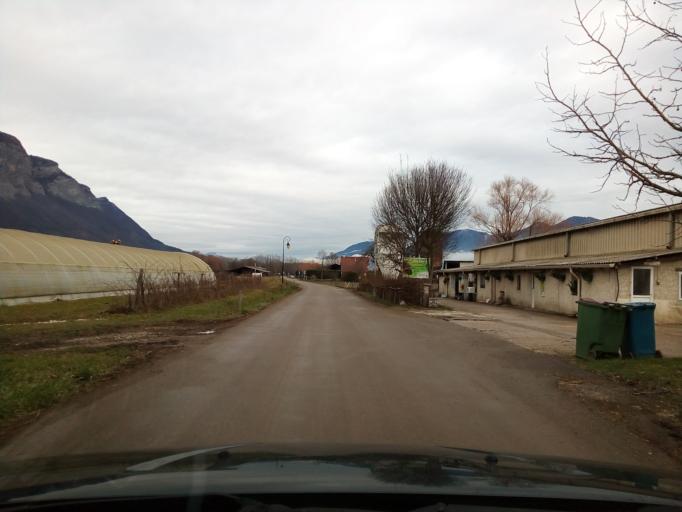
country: FR
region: Rhone-Alpes
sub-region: Departement de l'Isere
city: Crolles
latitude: 45.2807
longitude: 5.8948
